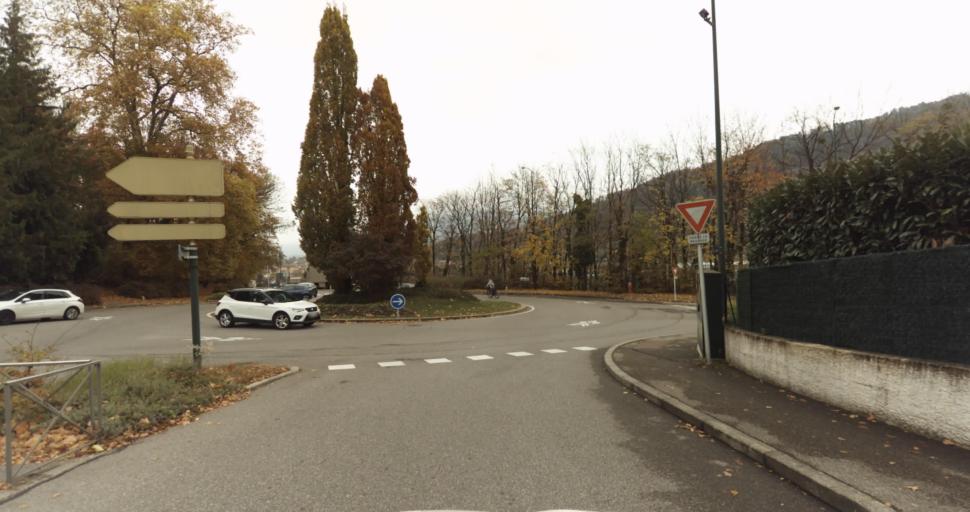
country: FR
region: Rhone-Alpes
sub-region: Departement de la Haute-Savoie
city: Annecy
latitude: 45.8871
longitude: 6.1114
